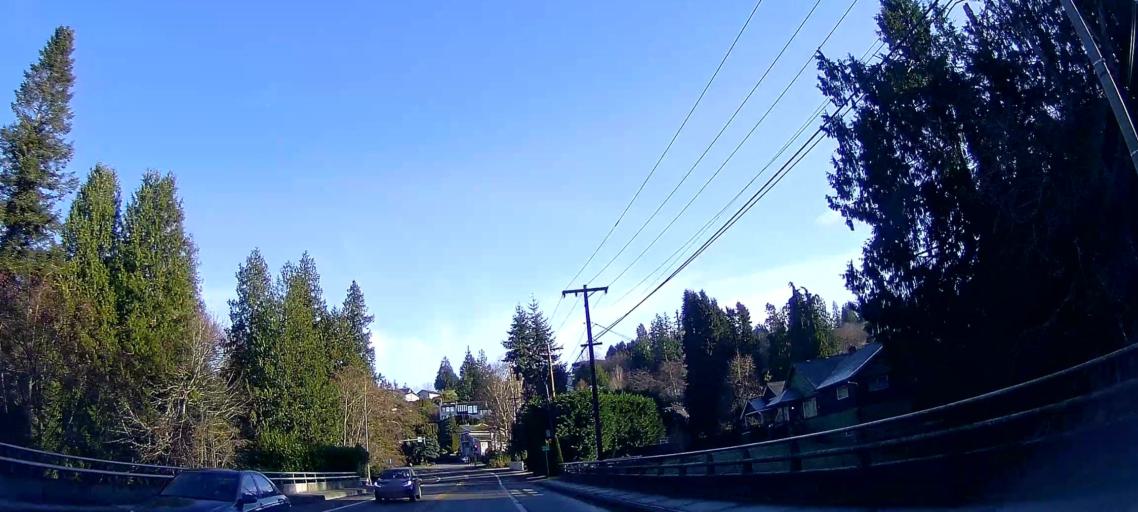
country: US
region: Washington
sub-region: Snohomish County
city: Everett
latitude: 47.9568
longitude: -122.2493
